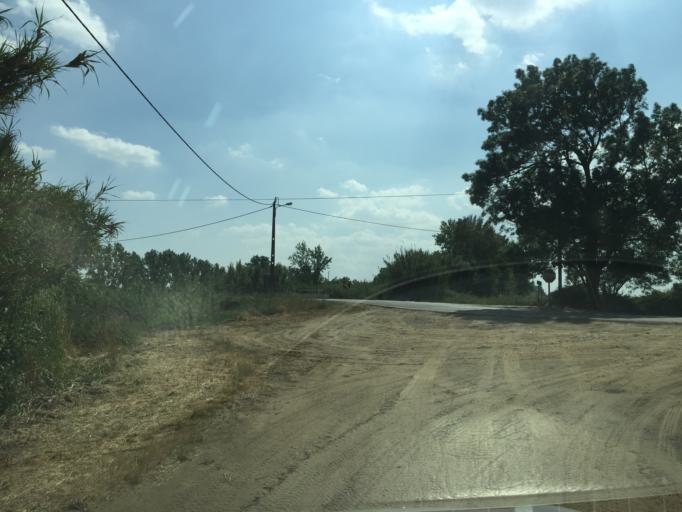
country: PT
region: Santarem
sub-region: Alpiarca
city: Alpiarca
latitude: 39.2938
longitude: -8.5235
